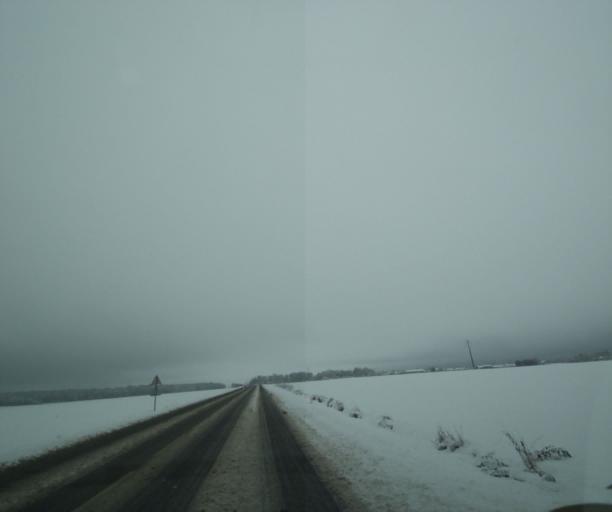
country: FR
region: Champagne-Ardenne
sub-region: Departement de la Haute-Marne
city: Wassy
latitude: 48.5574
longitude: 4.9256
